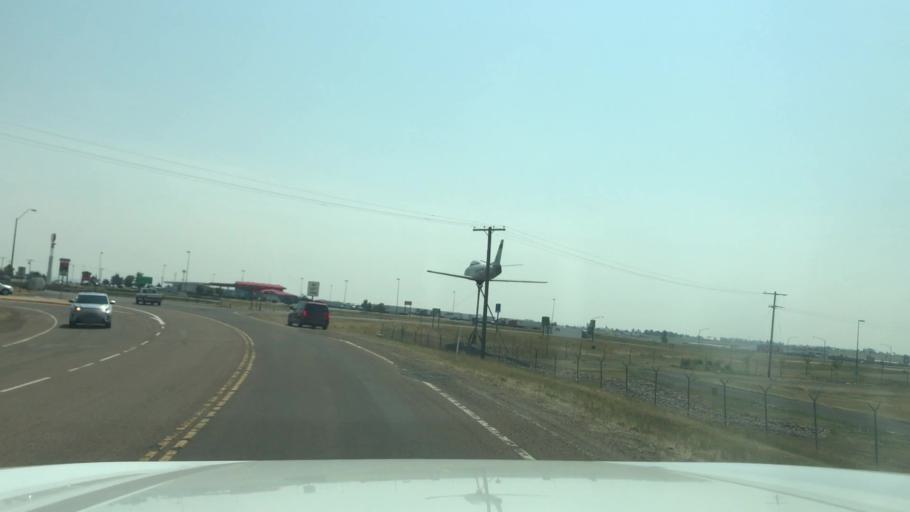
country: US
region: Montana
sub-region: Cascade County
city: Great Falls
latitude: 47.4739
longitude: -111.3623
